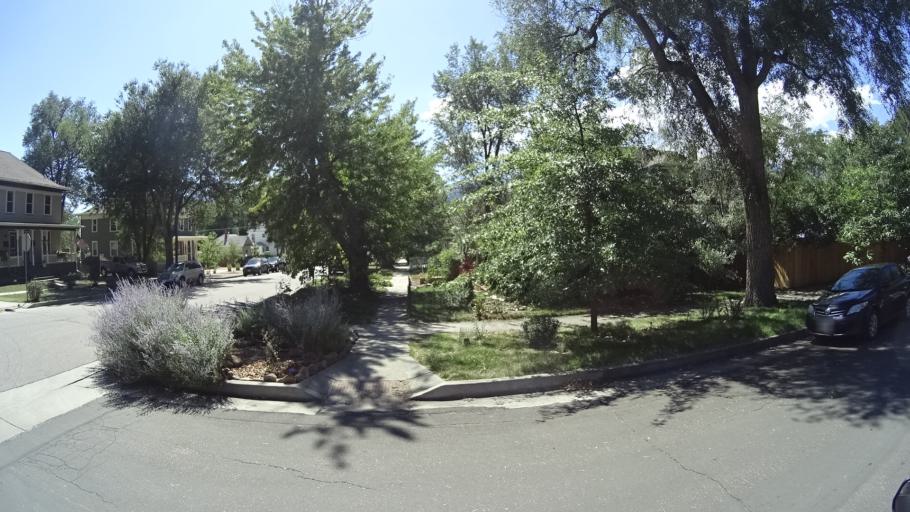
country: US
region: Colorado
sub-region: El Paso County
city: Colorado Springs
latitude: 38.8391
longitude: -104.8441
